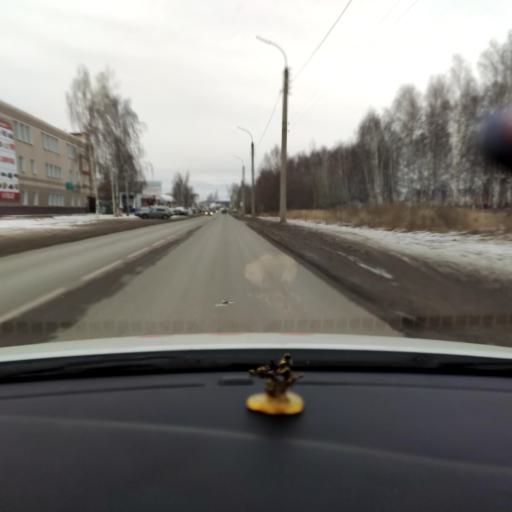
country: RU
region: Tatarstan
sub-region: Zelenodol'skiy Rayon
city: Zelenodolsk
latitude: 55.8642
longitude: 48.5484
